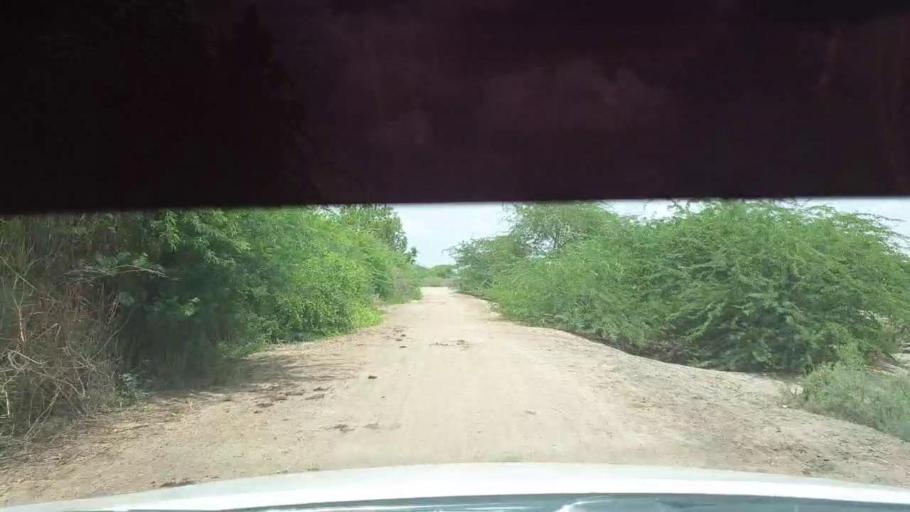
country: PK
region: Sindh
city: Kadhan
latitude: 24.4839
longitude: 69.0028
